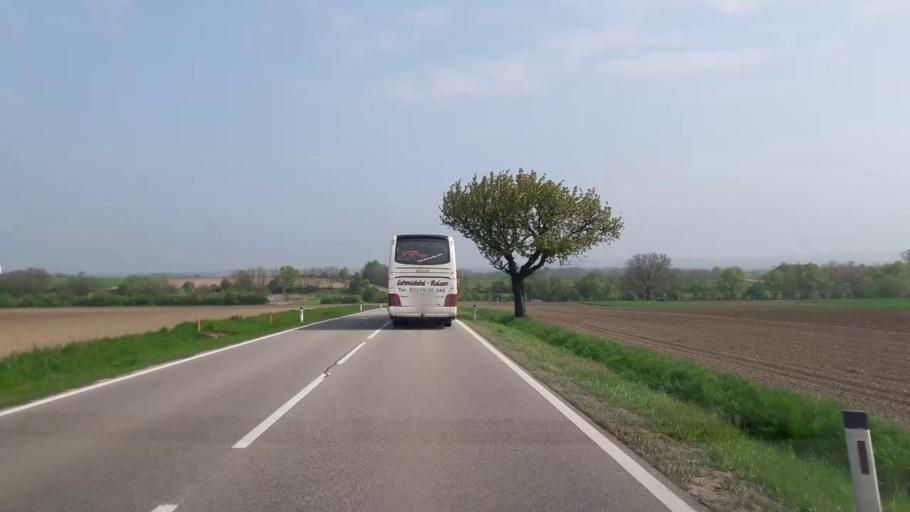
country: AT
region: Lower Austria
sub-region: Politischer Bezirk Hollabrunn
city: Wullersdorf
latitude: 48.6136
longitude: 16.0669
